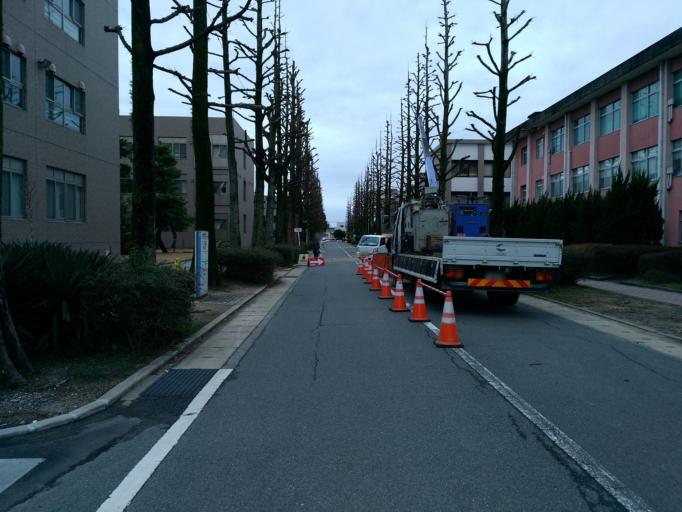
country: JP
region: Saga Prefecture
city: Saga-shi
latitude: 33.2441
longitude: 130.2925
